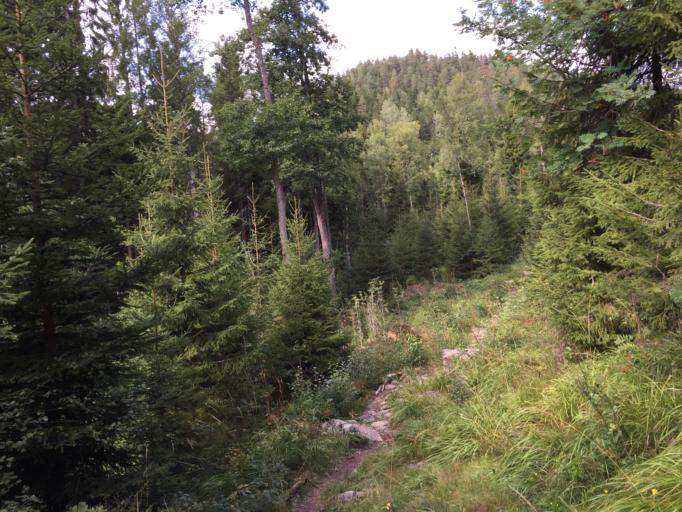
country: NO
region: Akershus
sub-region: Raelingen
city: Fjerdingby
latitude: 59.9102
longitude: 11.0376
